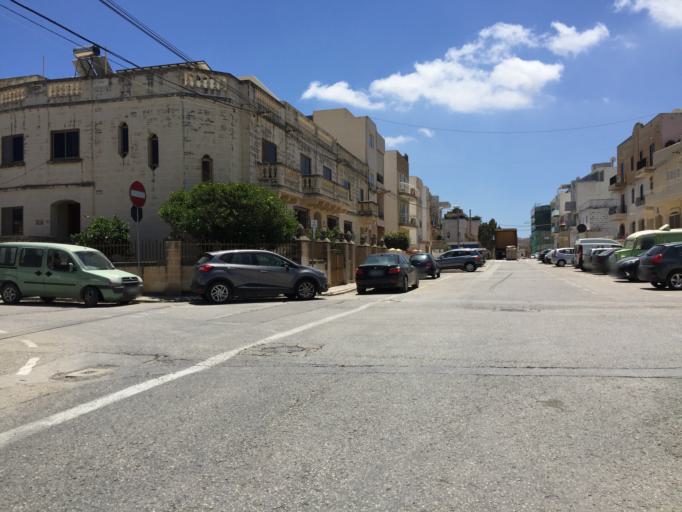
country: MT
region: Is-Swieqi
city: Swieqi
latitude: 35.9226
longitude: 14.4823
